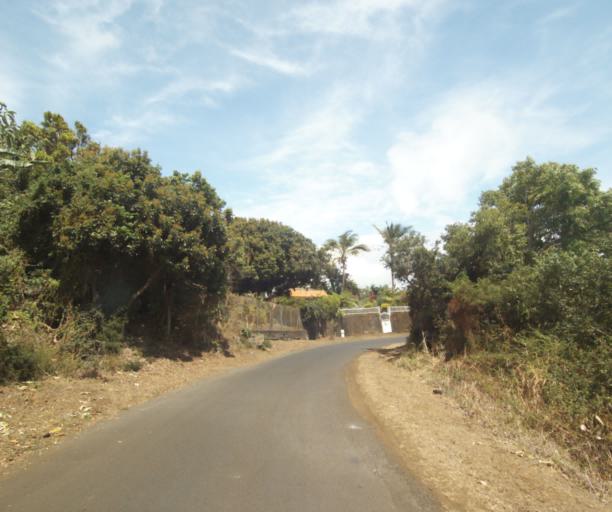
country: RE
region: Reunion
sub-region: Reunion
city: Trois-Bassins
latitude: -21.0959
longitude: 55.2766
